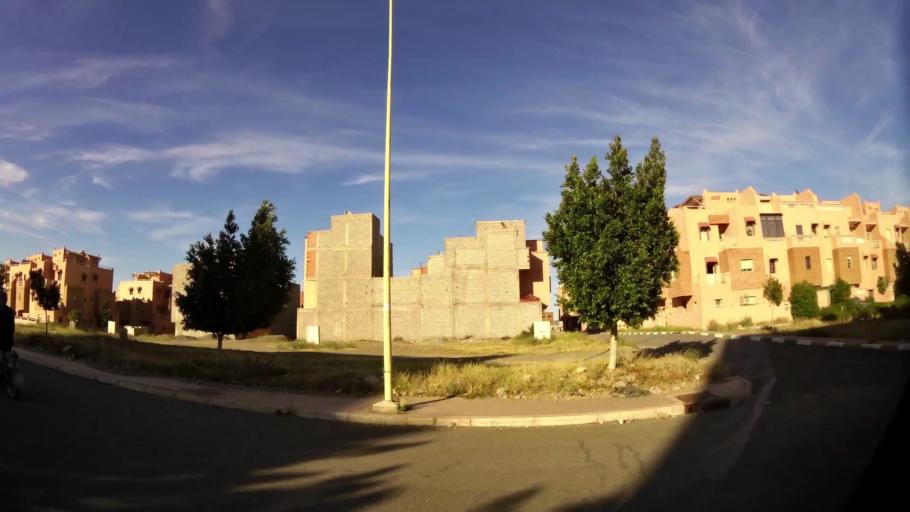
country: MA
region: Marrakech-Tensift-Al Haouz
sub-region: Marrakech
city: Marrakesh
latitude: 31.7570
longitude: -8.1020
